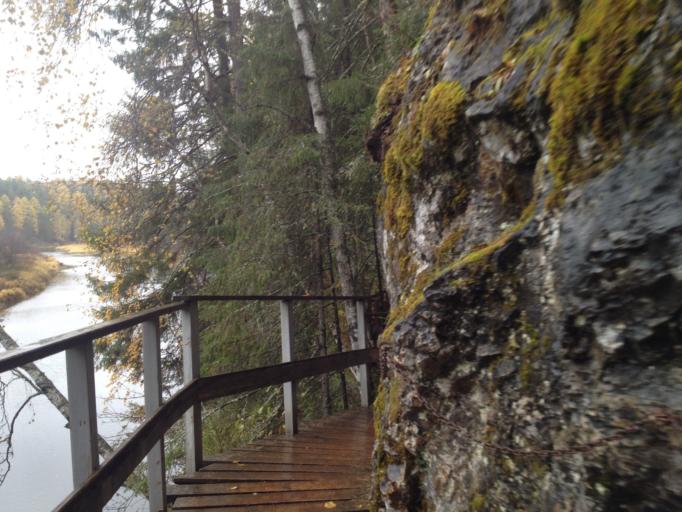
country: RU
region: Sverdlovsk
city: Mikhaylovsk
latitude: 56.5121
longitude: 59.2549
